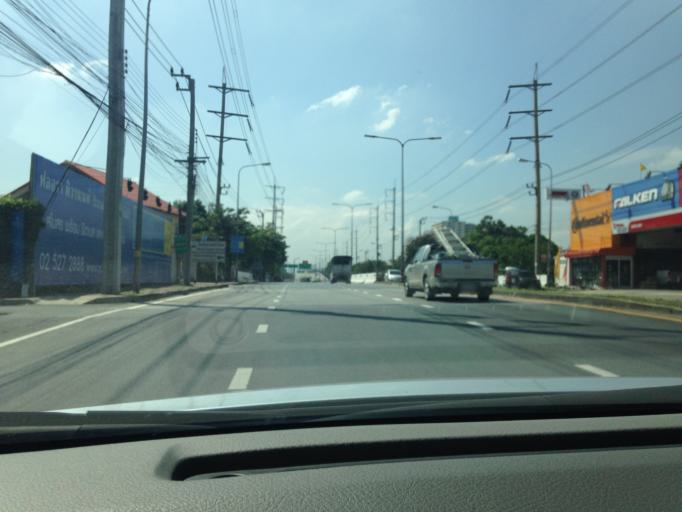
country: TH
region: Nonthaburi
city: Mueang Nonthaburi
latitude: 13.8491
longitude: 100.4999
